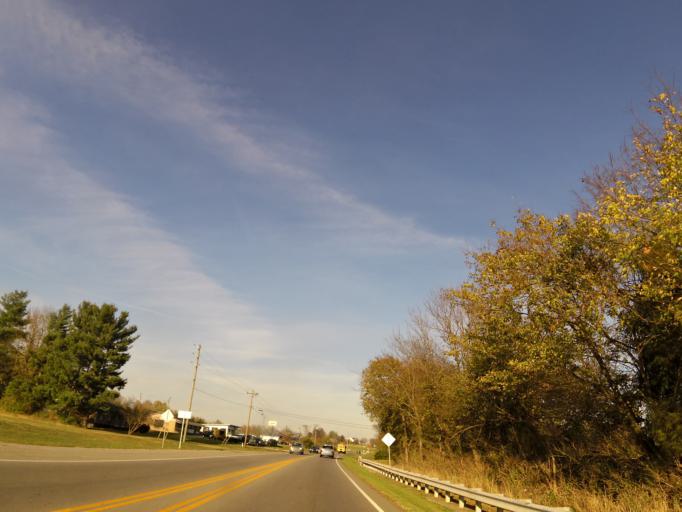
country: US
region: Kentucky
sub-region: Lincoln County
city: Stanford
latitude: 37.5495
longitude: -84.6448
